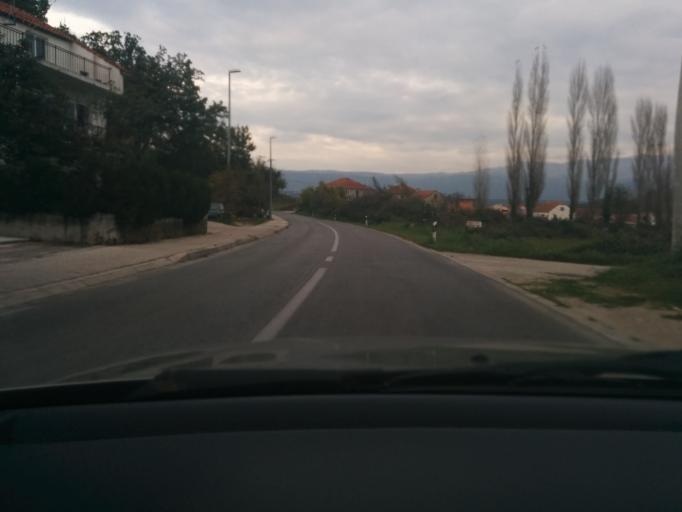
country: HR
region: Splitsko-Dalmatinska
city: Sinj
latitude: 43.7084
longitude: 16.6564
